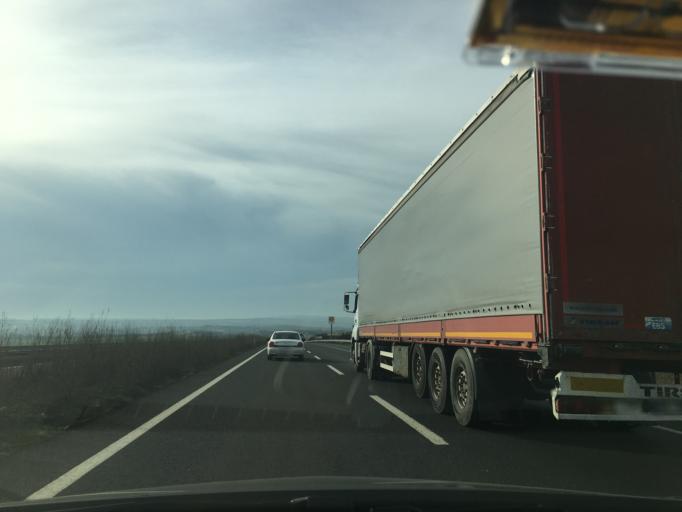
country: TR
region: Istanbul
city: Buyukcavuslu
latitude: 41.2594
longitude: 28.0360
